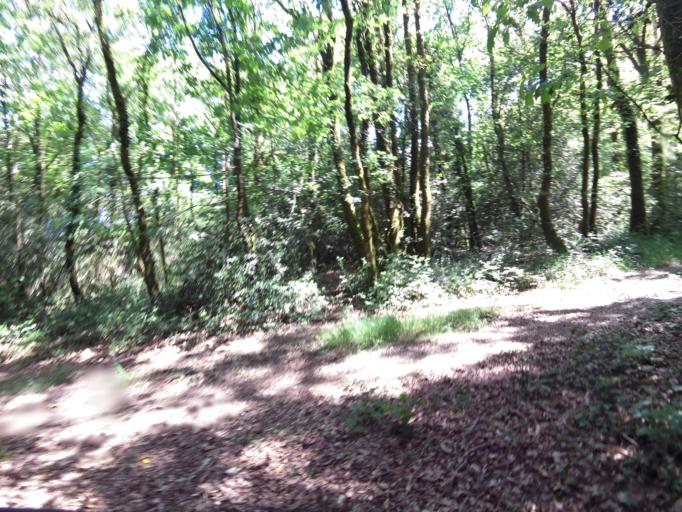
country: FR
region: Brittany
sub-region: Departement du Morbihan
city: Molac
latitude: 47.7144
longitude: -2.4212
